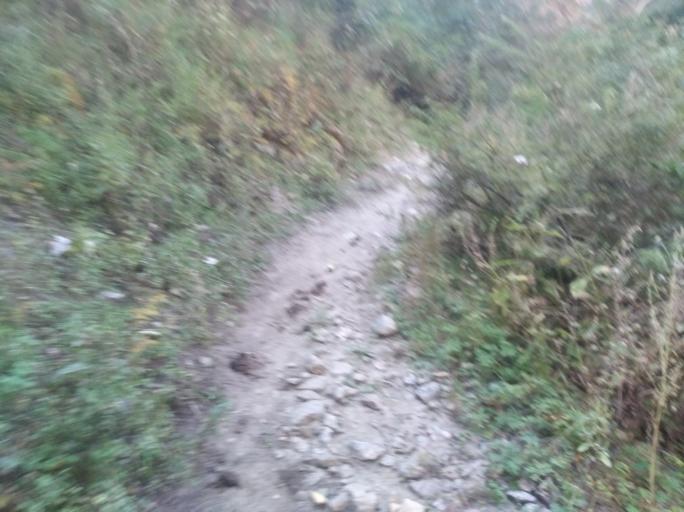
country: NP
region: Western Region
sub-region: Dhawalagiri Zone
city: Jomsom
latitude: 28.8776
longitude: 83.0232
